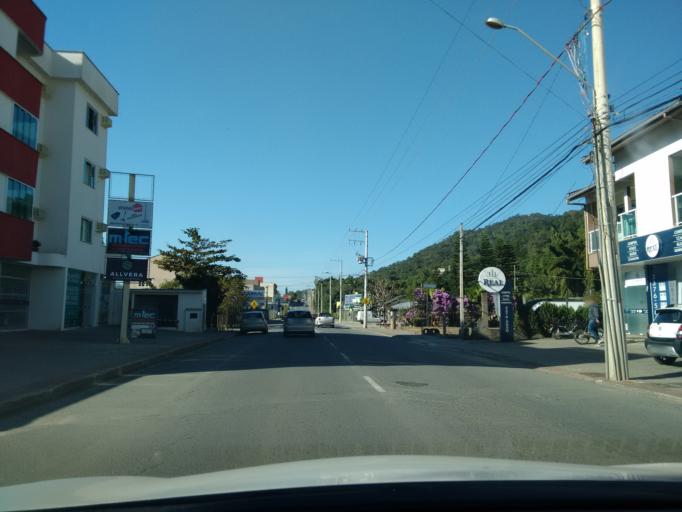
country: BR
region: Santa Catarina
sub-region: Jaragua Do Sul
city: Jaragua do Sul
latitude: -26.5131
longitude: -49.1171
